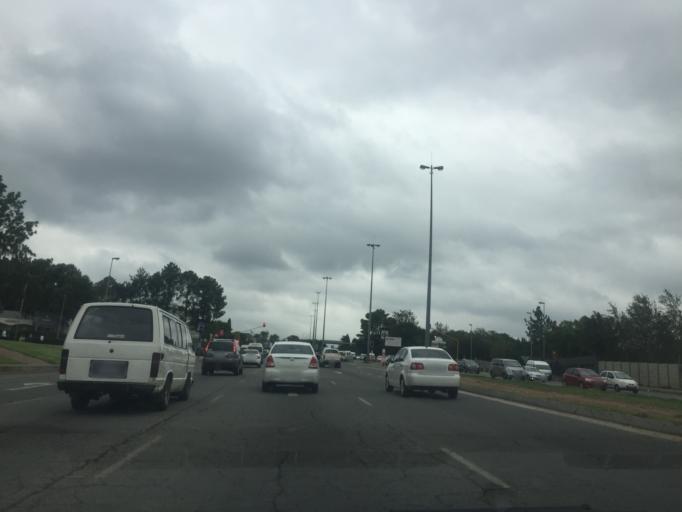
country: ZA
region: Gauteng
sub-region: City of Johannesburg Metropolitan Municipality
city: Diepsloot
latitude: -26.0257
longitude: 28.0093
